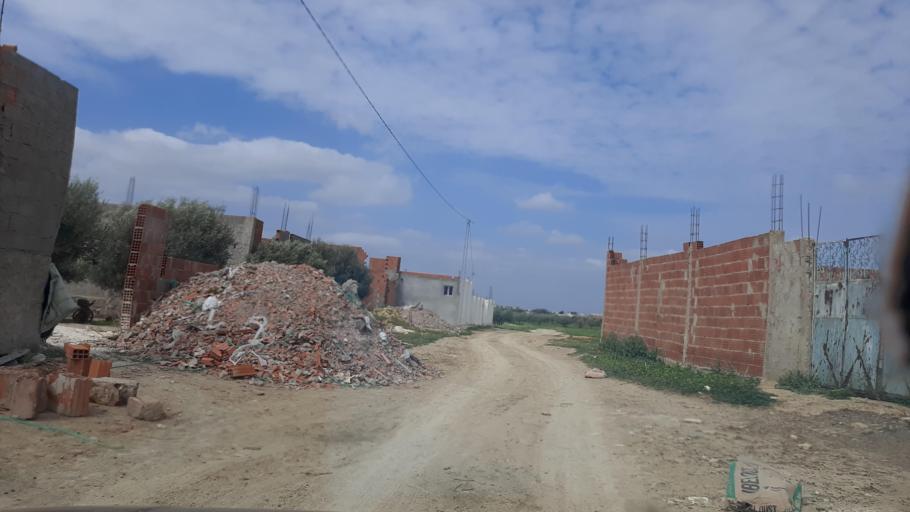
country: TN
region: Tunis
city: Oued Lill
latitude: 36.6873
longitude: 9.9974
